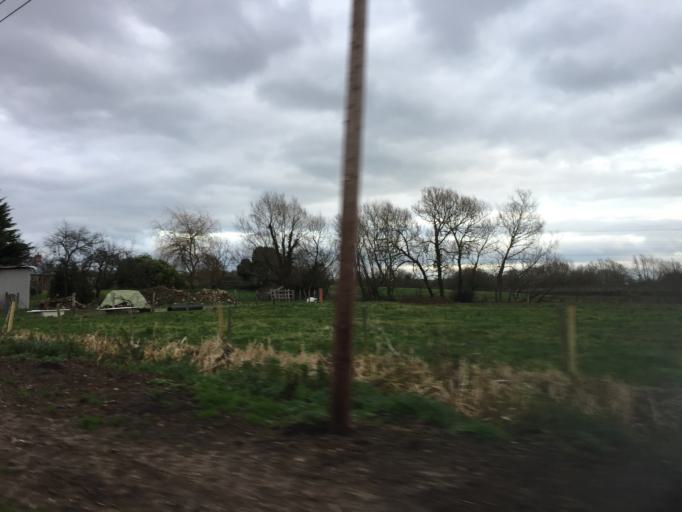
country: GB
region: Wales
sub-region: Monmouthshire
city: Magor
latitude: 51.5759
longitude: -2.8508
